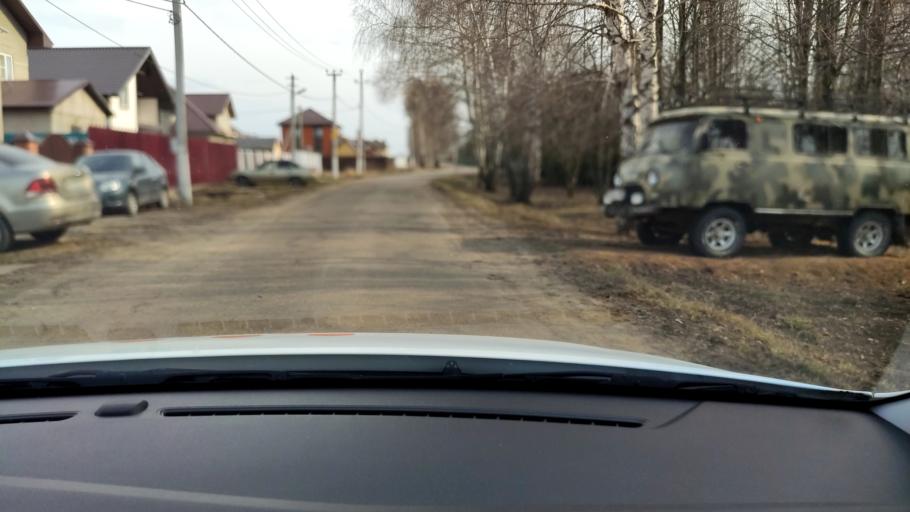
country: RU
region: Tatarstan
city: Stolbishchi
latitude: 55.6446
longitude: 49.3125
